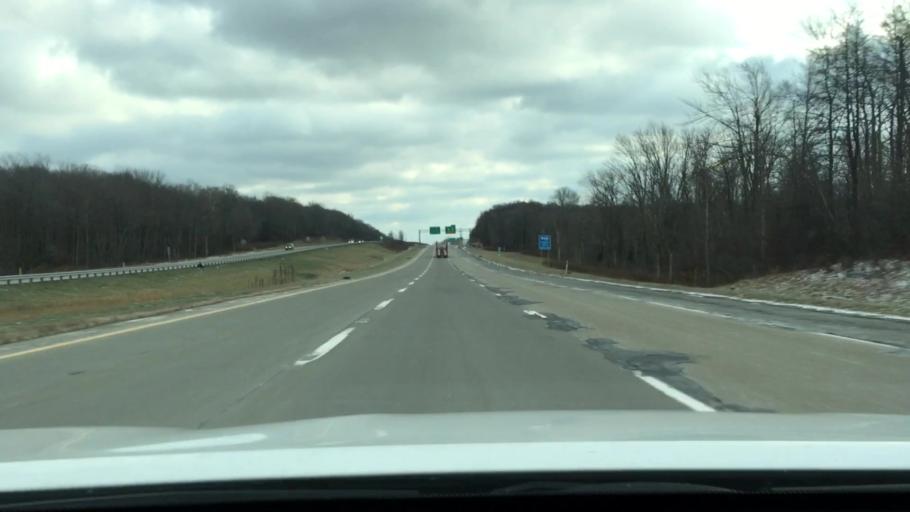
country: US
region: Pennsylvania
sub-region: Monroe County
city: Pocono Pines
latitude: 41.1912
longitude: -75.4440
